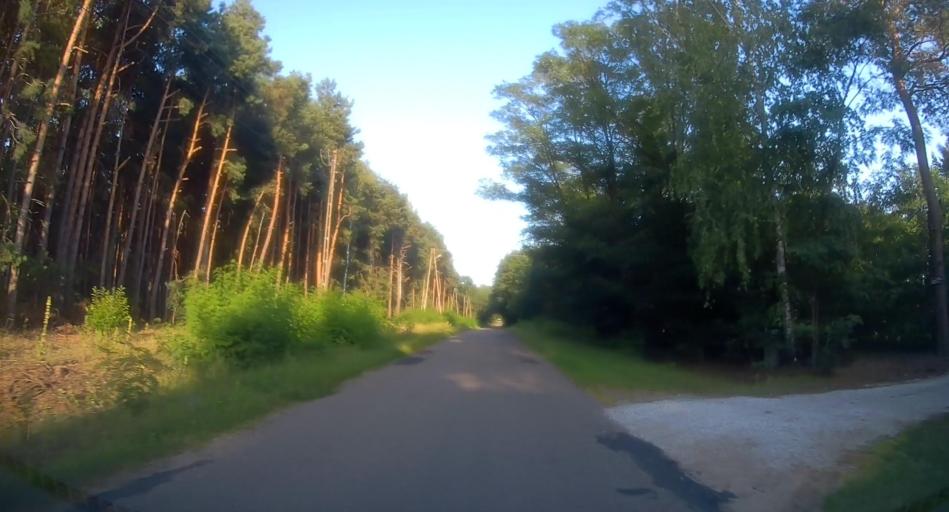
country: PL
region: Lodz Voivodeship
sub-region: Powiat skierniewicki
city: Kowiesy
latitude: 51.9046
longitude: 20.3562
